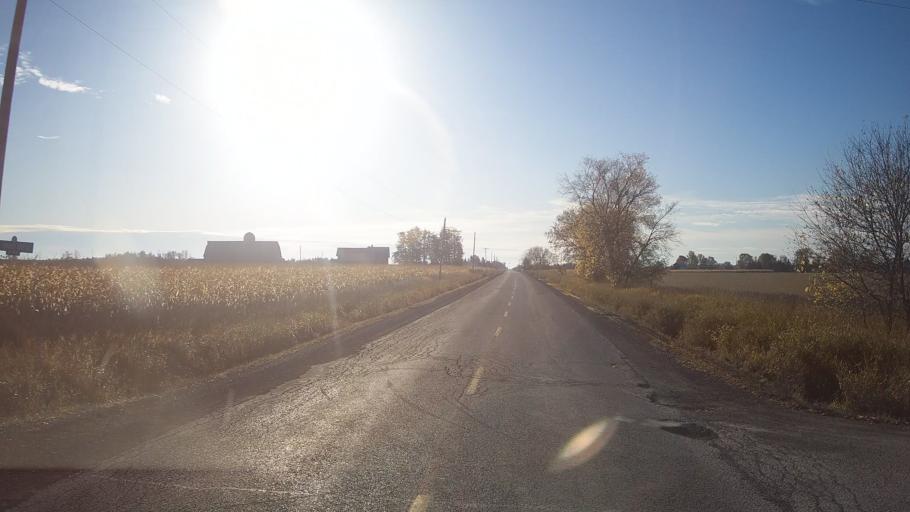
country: CA
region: Ontario
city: Arnprior
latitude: 45.3630
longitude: -76.2471
